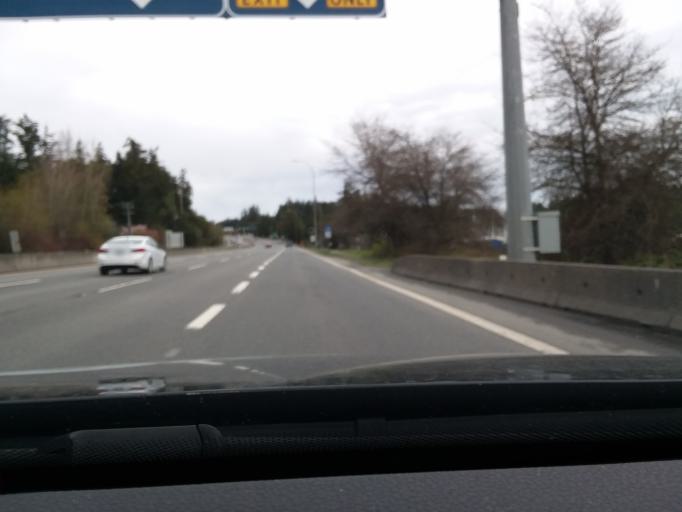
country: CA
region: British Columbia
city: North Saanich
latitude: 48.6790
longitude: -123.4204
